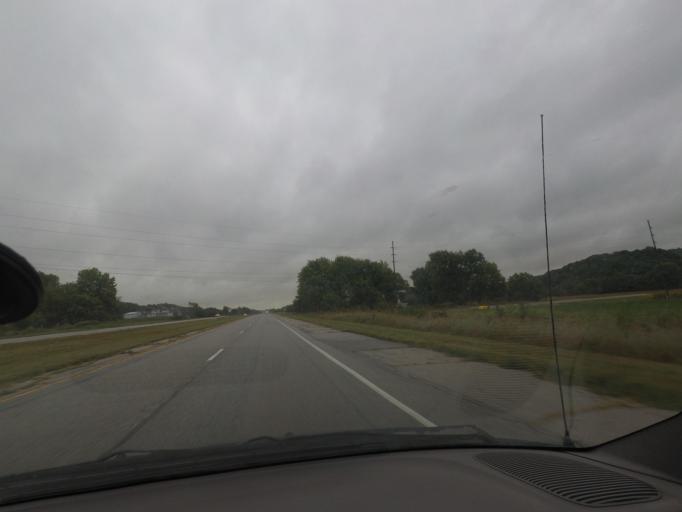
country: US
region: Illinois
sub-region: Adams County
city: Payson
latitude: 39.7193
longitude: -91.1775
